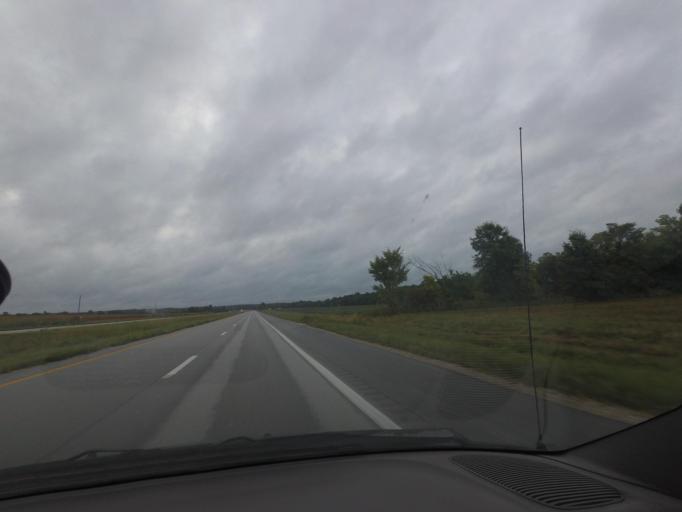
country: US
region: Missouri
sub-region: Shelby County
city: Shelbina
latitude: 39.6667
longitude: -91.9225
